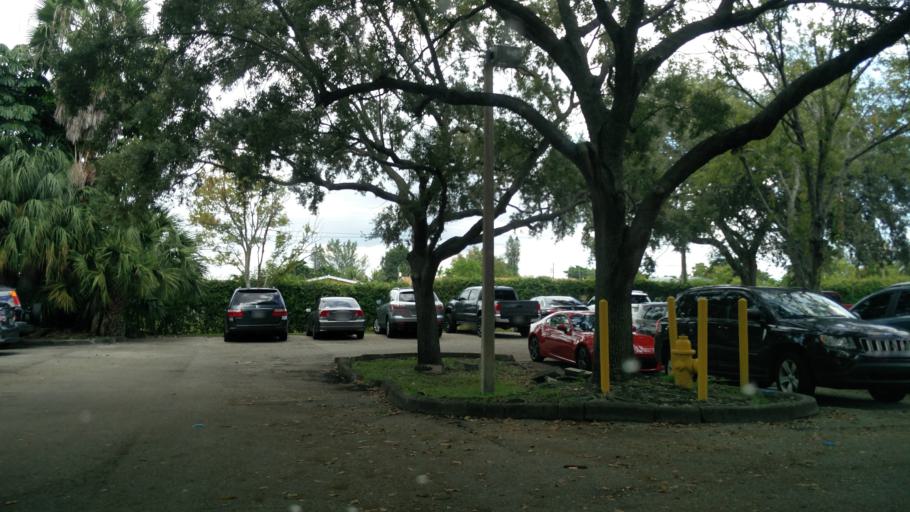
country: US
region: Florida
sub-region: Broward County
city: Plantation
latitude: 26.1496
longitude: -80.2448
